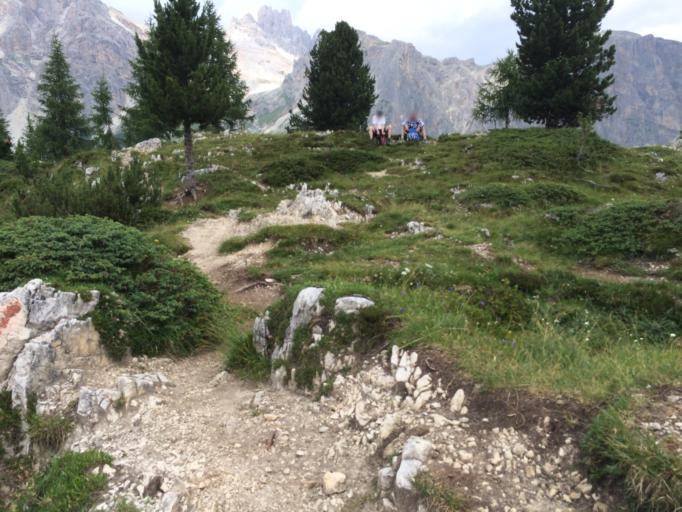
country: IT
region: Veneto
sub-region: Provincia di Belluno
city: Colle Santa Lucia
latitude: 46.5117
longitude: 12.0231
